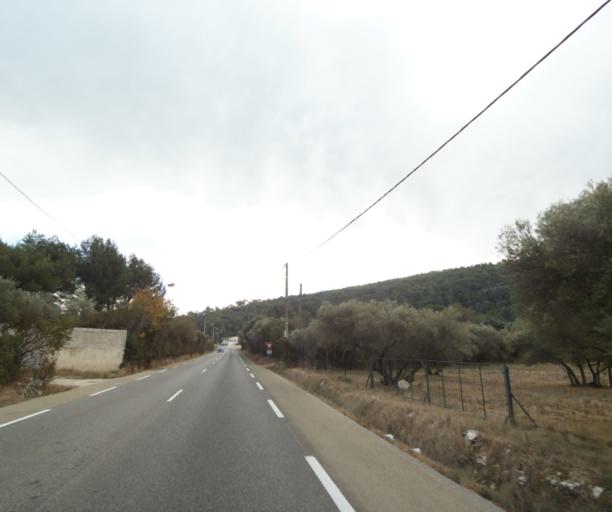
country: FR
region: Provence-Alpes-Cote d'Azur
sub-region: Departement des Bouches-du-Rhone
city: Gemenos
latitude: 43.2756
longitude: 5.6355
